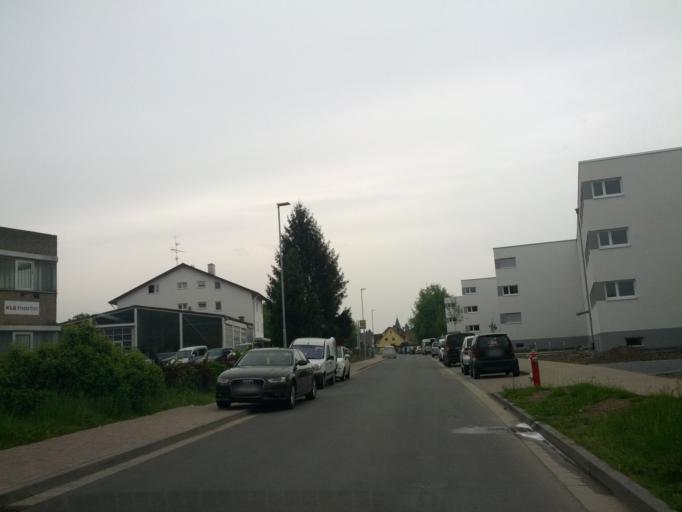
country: DE
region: Baden-Wuerttemberg
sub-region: Freiburg Region
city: Umkirch
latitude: 48.0380
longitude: 7.7612
